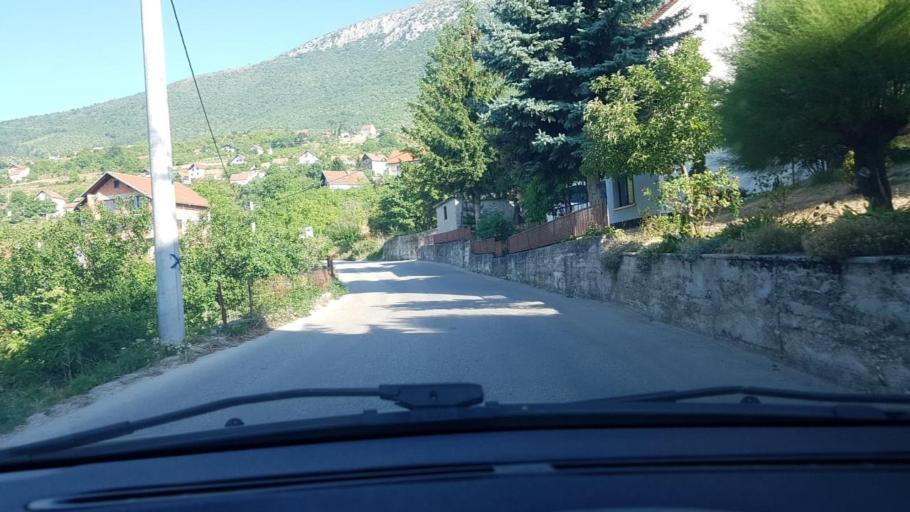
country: BA
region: Federation of Bosnia and Herzegovina
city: Rumboci
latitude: 43.8292
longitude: 17.5048
